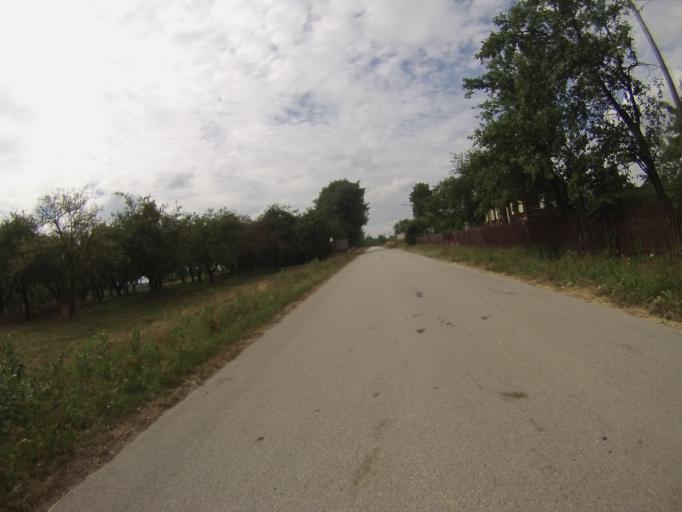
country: PL
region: Swietokrzyskie
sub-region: Powiat kielecki
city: Lagow
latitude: 50.7416
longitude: 21.1167
